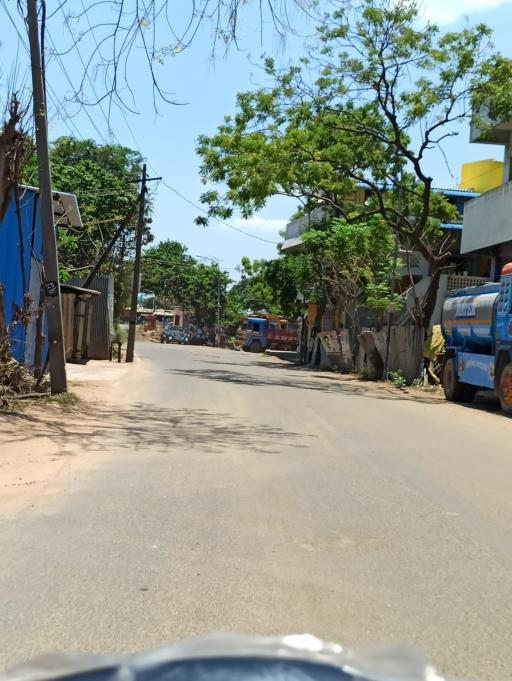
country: IN
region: Tamil Nadu
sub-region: Thiruvallur
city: Chinnasekkadu
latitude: 13.1630
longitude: 80.2289
